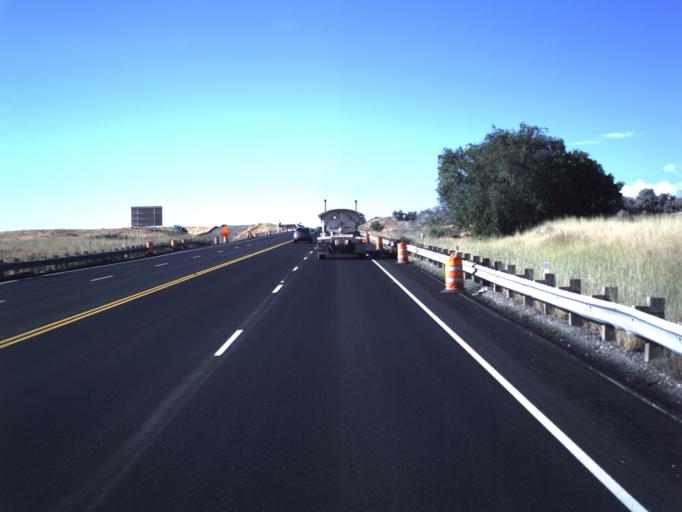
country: US
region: Utah
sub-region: Salt Lake County
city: Magna
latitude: 40.6754
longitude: -112.0920
